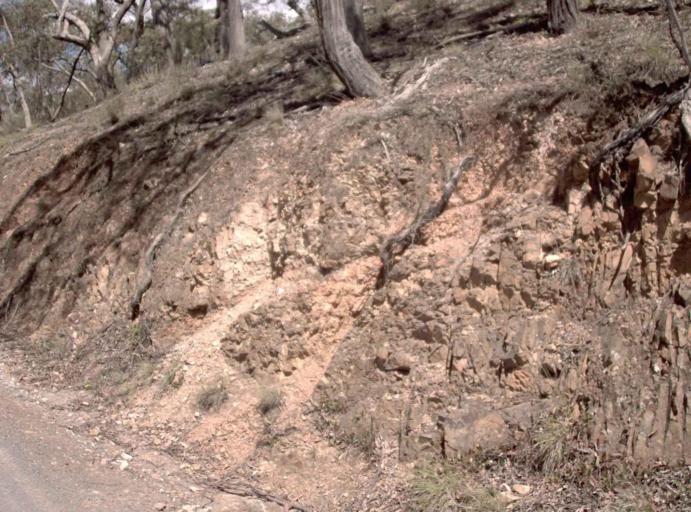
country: AU
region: New South Wales
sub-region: Bombala
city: Bombala
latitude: -37.1046
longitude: 148.6394
